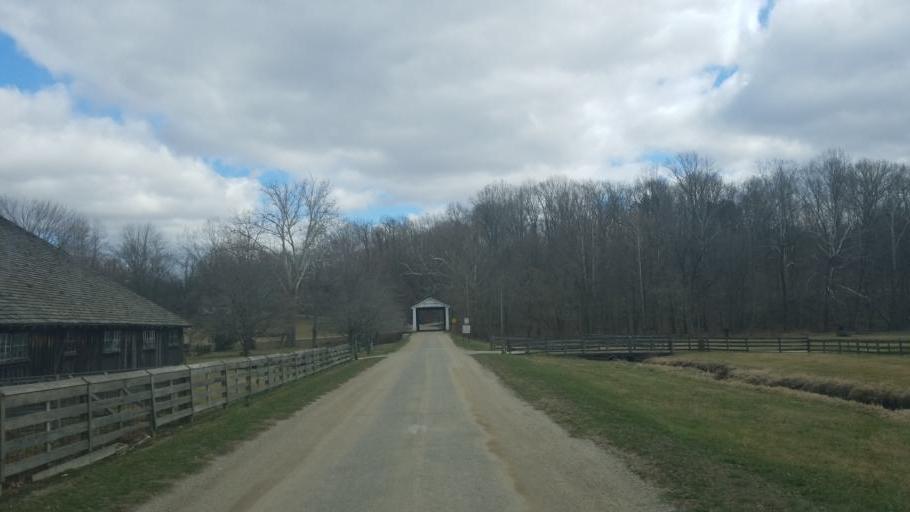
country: US
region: Indiana
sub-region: Parke County
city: Rockville
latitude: 39.7618
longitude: -87.2079
